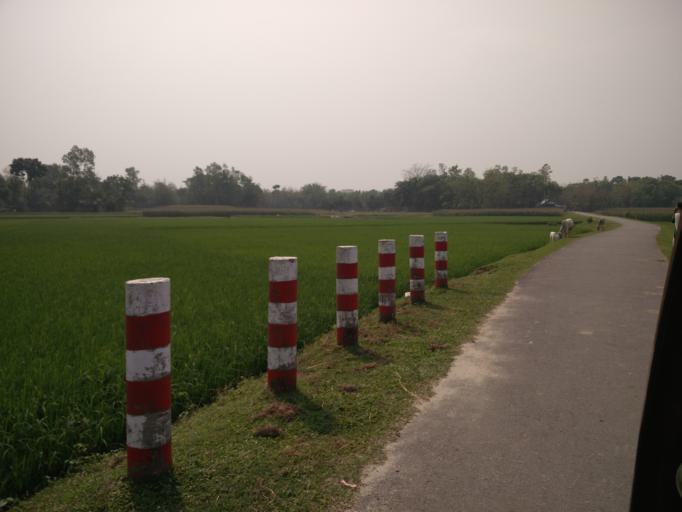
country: BD
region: Dhaka
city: Muktagacha
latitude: 24.9022
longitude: 90.2588
